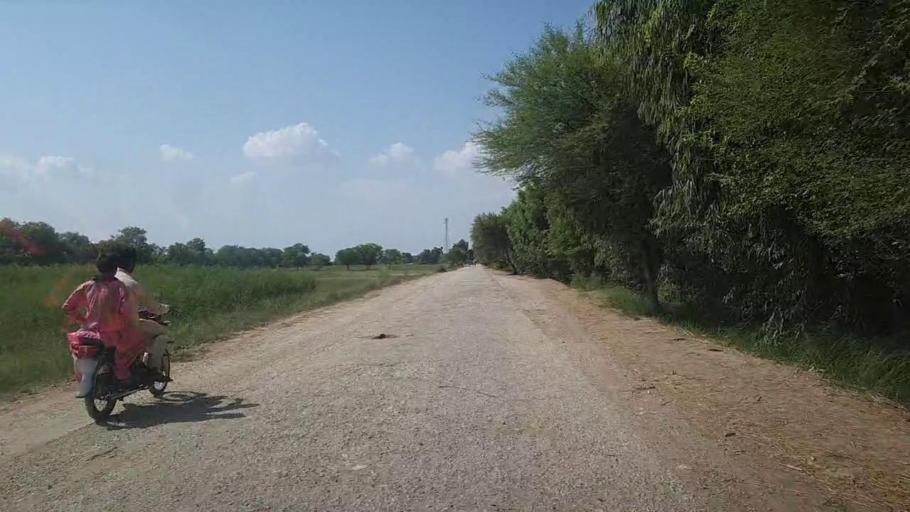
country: PK
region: Sindh
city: Khairpur
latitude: 28.1151
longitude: 69.6183
